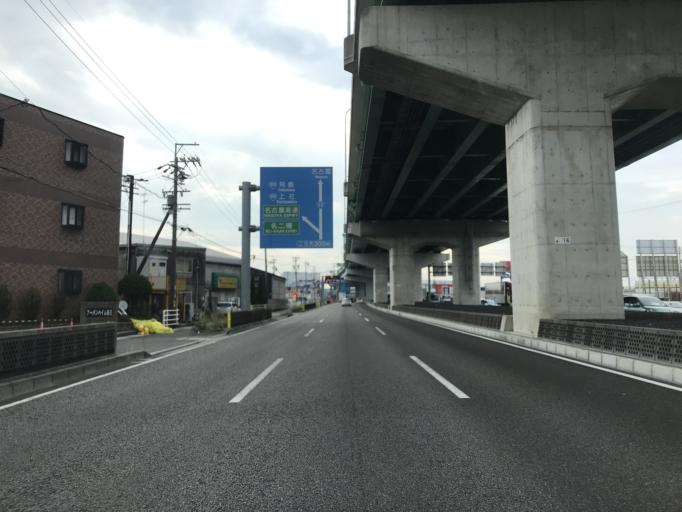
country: JP
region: Aichi
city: Iwakura
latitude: 35.2278
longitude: 136.8526
